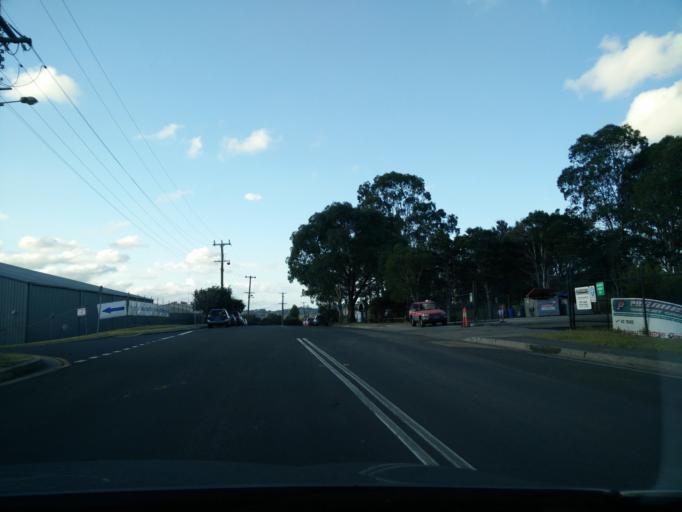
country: AU
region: New South Wales
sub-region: Wollongong
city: Cordeaux Heights
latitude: -34.4594
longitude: 150.8455
